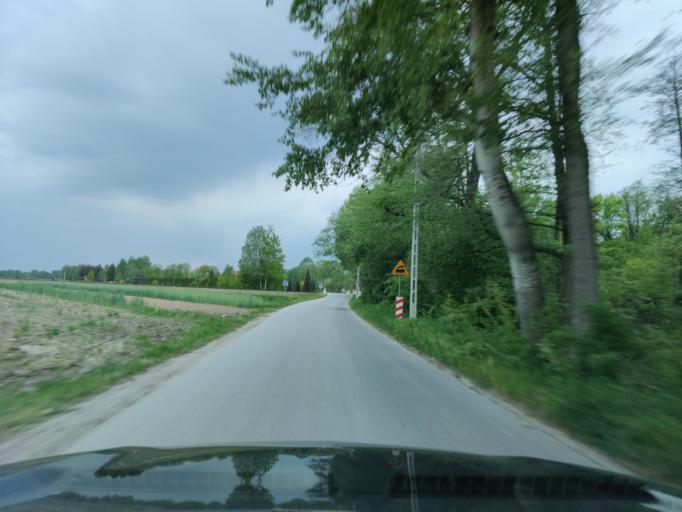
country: PL
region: Masovian Voivodeship
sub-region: Powiat piaseczynski
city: Konstancin-Jeziorna
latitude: 52.1227
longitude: 21.1553
